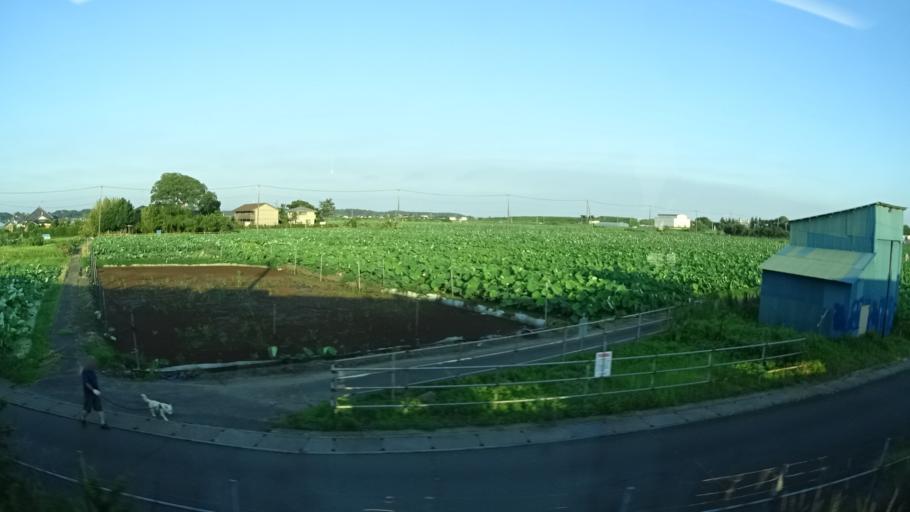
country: JP
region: Ibaraki
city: Ami
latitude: 36.0925
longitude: 140.2141
